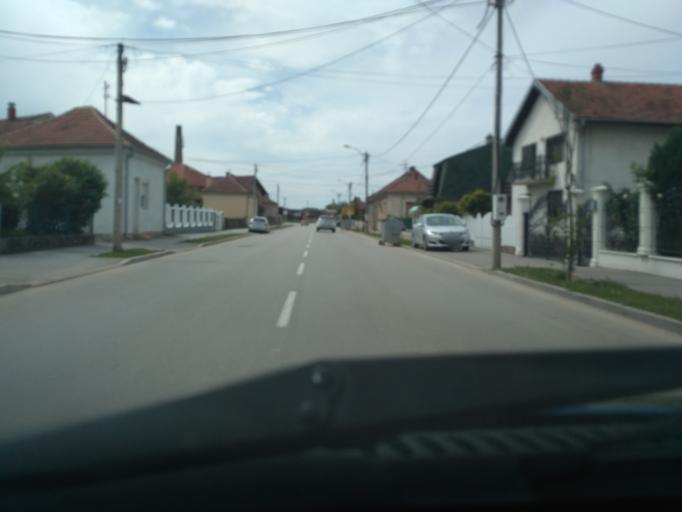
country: RS
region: Central Serbia
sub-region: Pomoravski Okrug
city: Svilajnac
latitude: 44.2354
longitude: 21.1907
